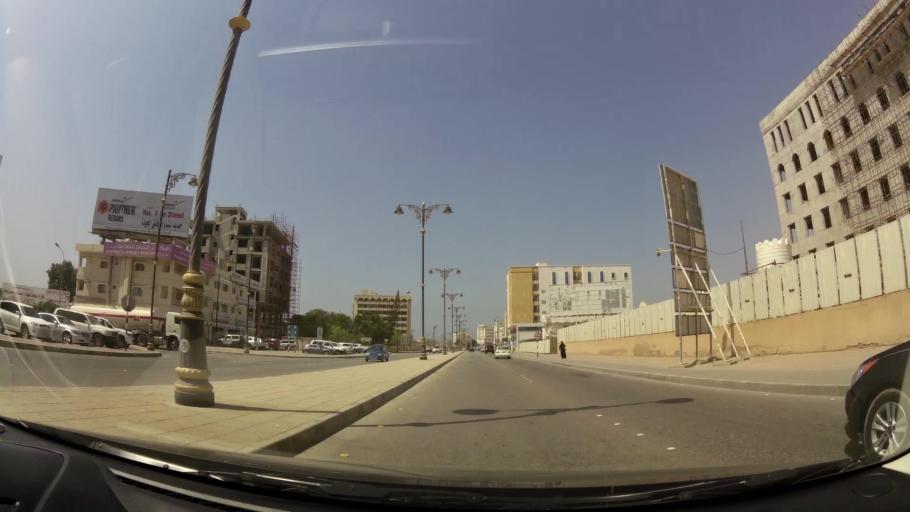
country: OM
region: Zufar
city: Salalah
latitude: 17.0232
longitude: 54.1112
